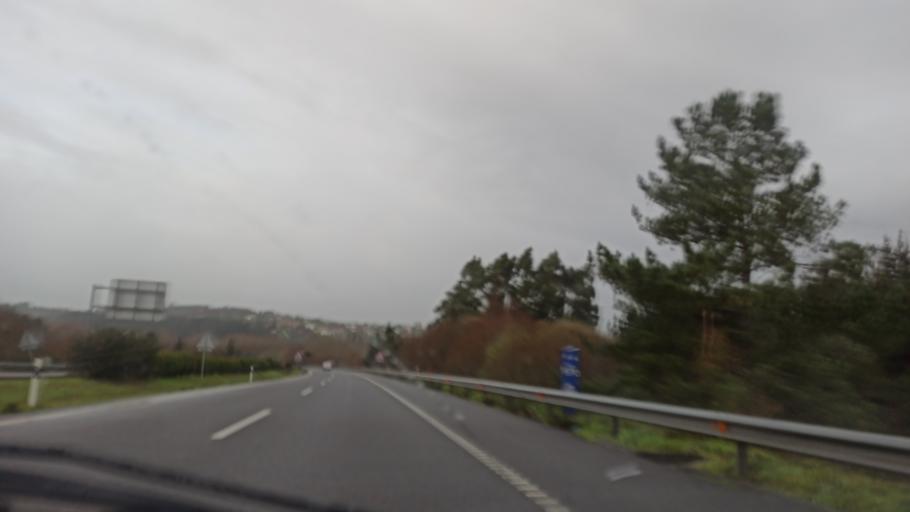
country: ES
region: Galicia
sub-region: Provincia da Coruna
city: Betanzos
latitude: 43.2622
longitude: -8.2505
